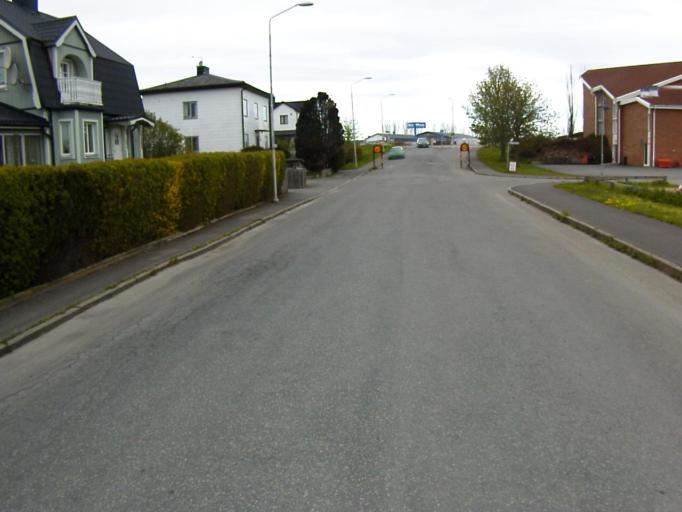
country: SE
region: Skane
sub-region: Kristianstads Kommun
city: Kristianstad
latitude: 56.0196
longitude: 14.1384
